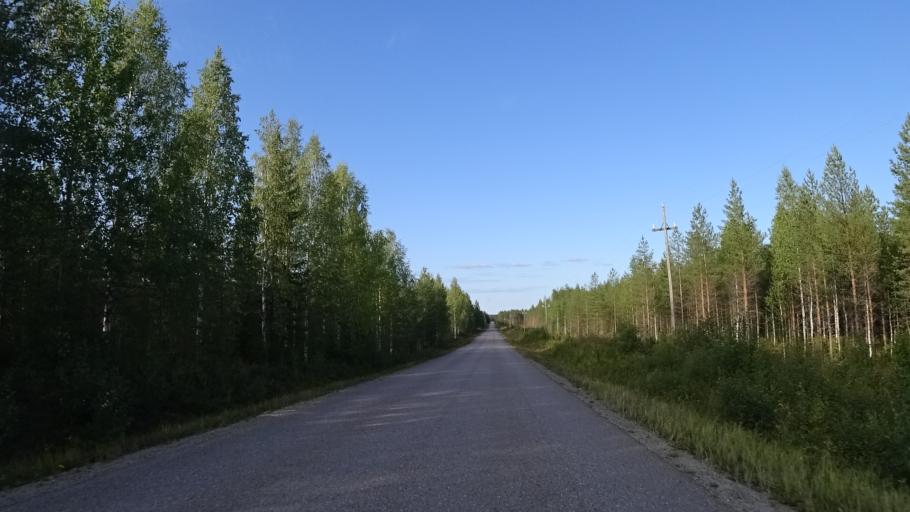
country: FI
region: North Karelia
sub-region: Joensuu
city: Eno
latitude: 63.0711
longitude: 30.5683
